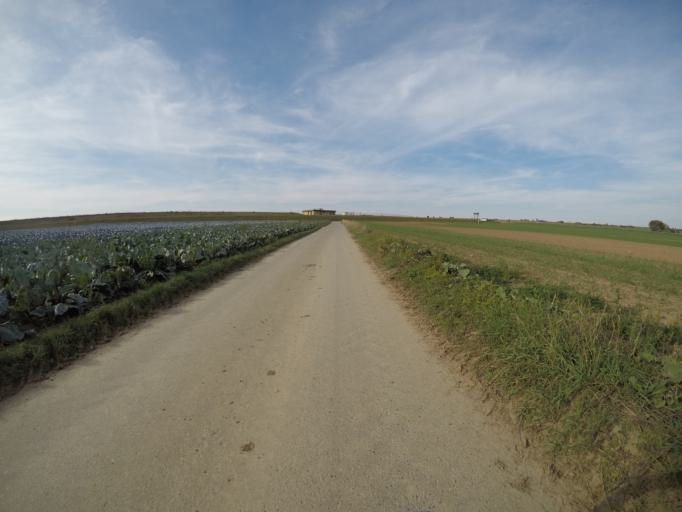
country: DE
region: Baden-Wuerttemberg
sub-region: Regierungsbezirk Stuttgart
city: Neuhausen auf den Fildern
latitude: 48.6912
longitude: 9.2487
